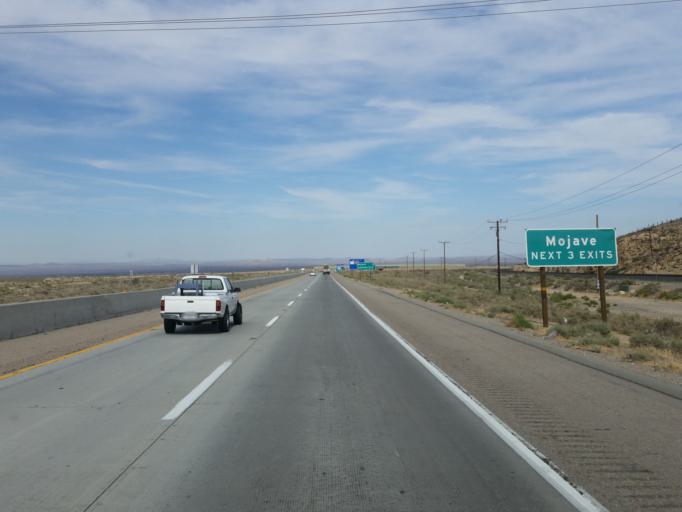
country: US
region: California
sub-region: Kern County
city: Mojave
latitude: 35.1165
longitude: -118.1997
